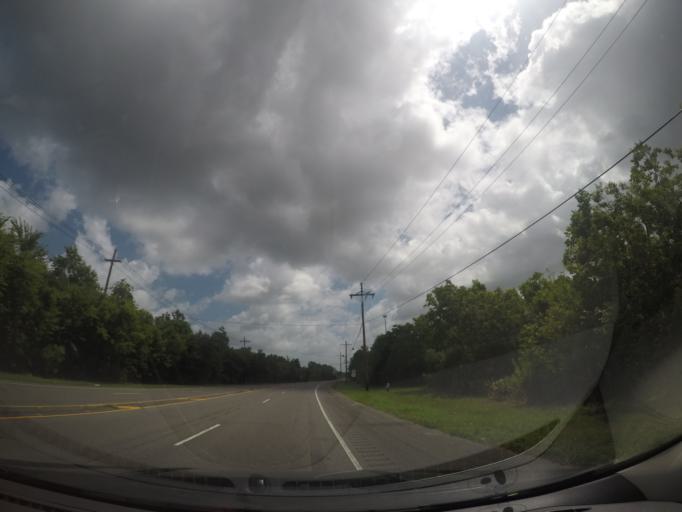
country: US
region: Louisiana
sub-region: Saint Bernard Parish
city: Meraux
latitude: 30.0720
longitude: -89.8635
